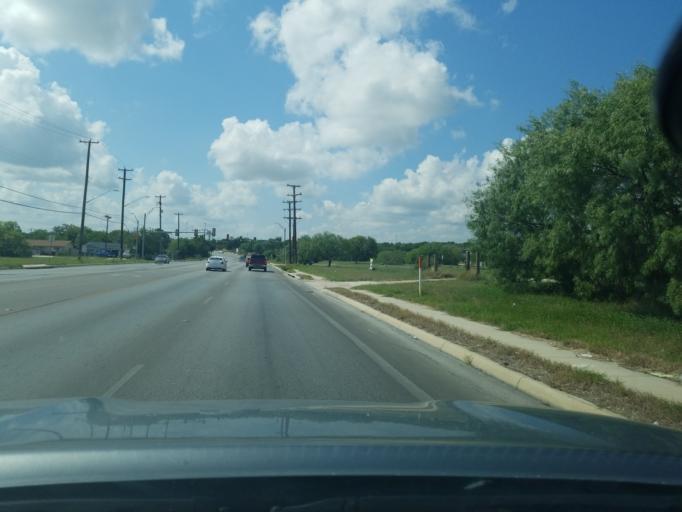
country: US
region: Texas
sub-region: Bexar County
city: San Antonio
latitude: 29.3369
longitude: -98.5342
